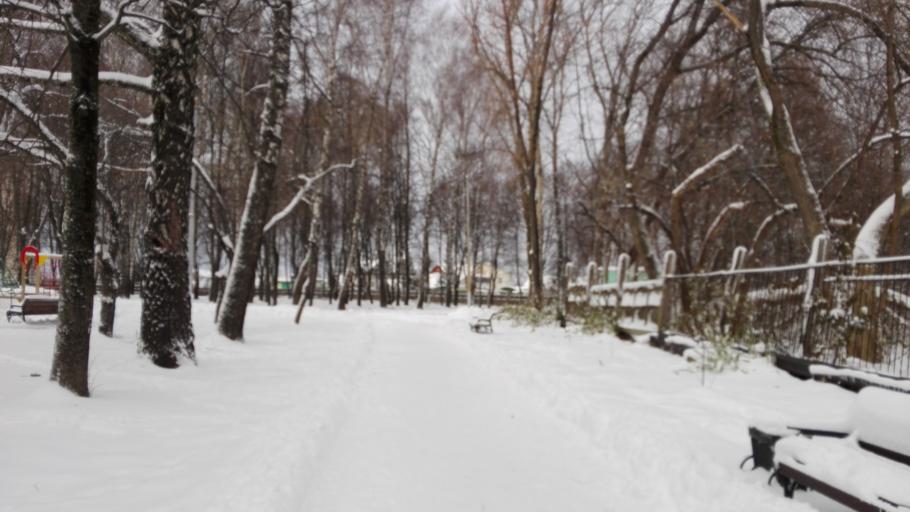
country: RU
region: Tula
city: Kosaya Gora
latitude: 54.1216
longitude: 37.5437
